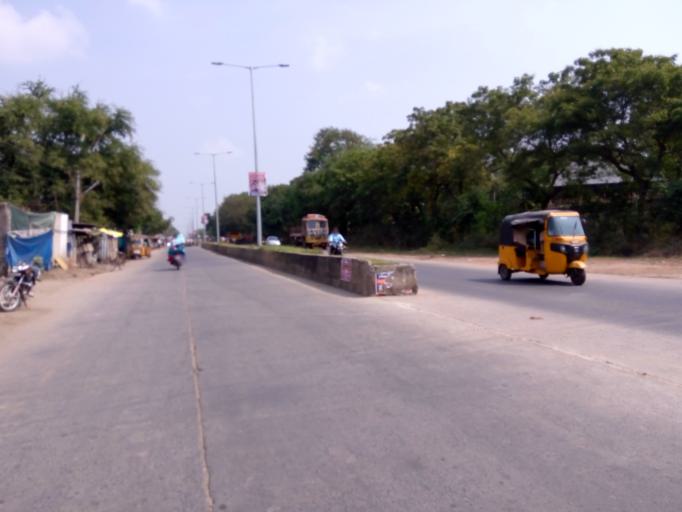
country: IN
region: Andhra Pradesh
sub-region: Prakasam
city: Chirala
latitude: 15.8385
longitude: 80.3678
